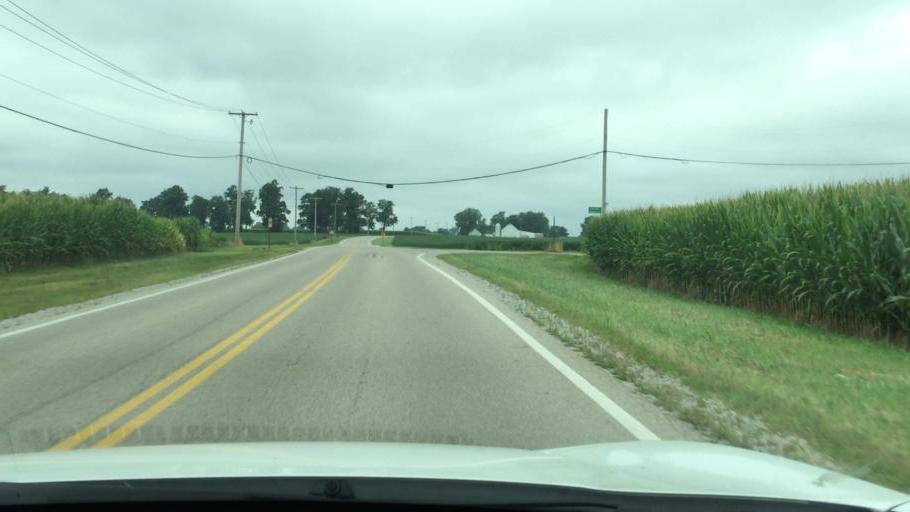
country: US
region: Ohio
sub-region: Clark County
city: Lisbon
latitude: 39.9415
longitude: -83.6617
